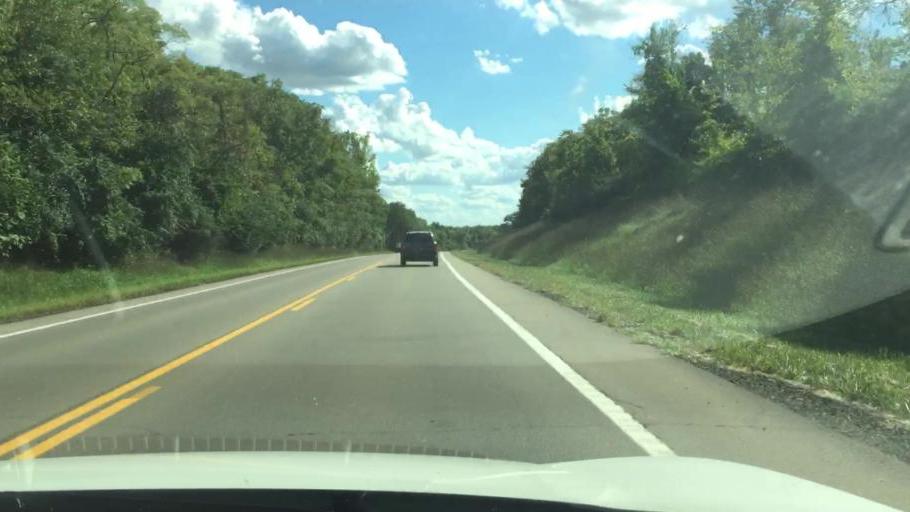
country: US
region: Ohio
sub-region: Clark County
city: Northridge
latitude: 39.9905
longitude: -83.7309
